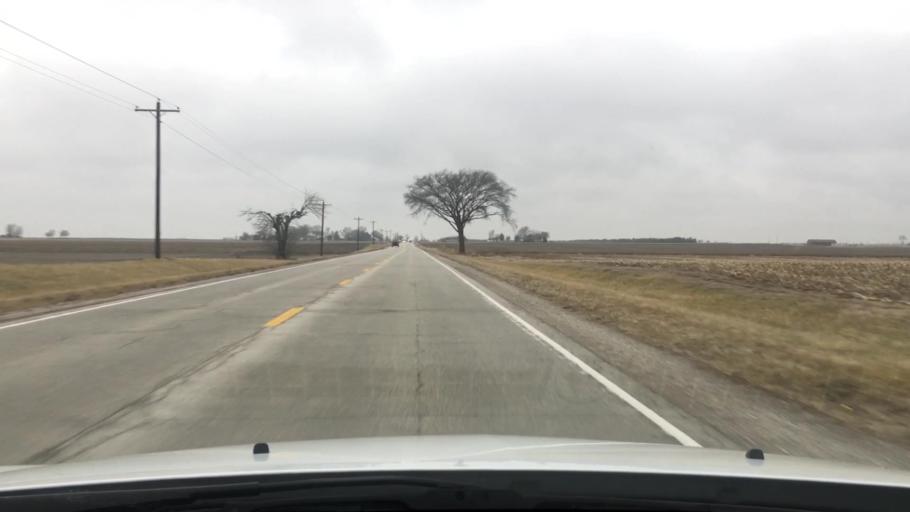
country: US
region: Illinois
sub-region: Iroquois County
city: Clifton
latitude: 40.8875
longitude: -87.8539
